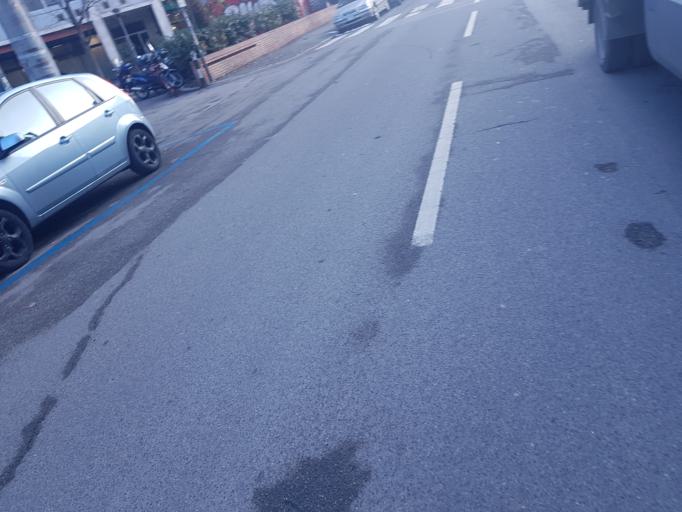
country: IT
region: Emilia-Romagna
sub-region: Provincia di Bologna
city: Bologna
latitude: 44.5038
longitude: 11.3385
